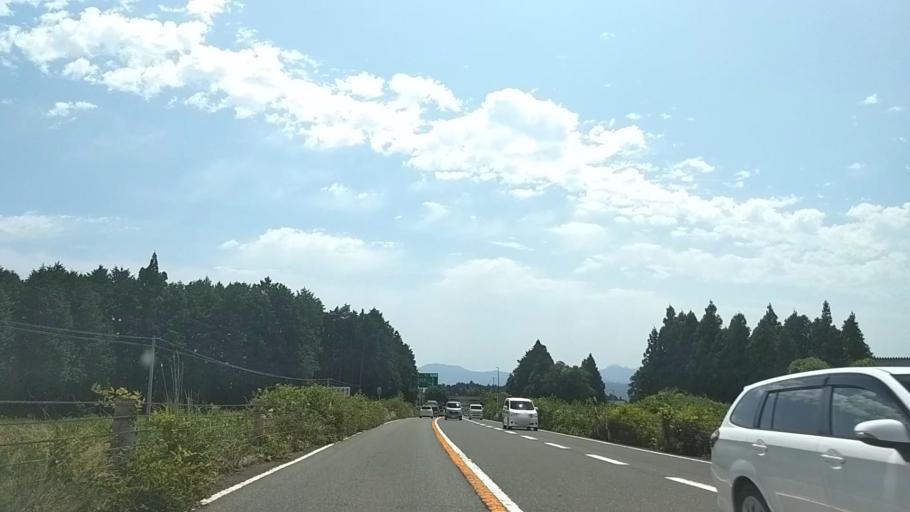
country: JP
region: Shizuoka
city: Fujinomiya
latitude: 35.2813
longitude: 138.6127
